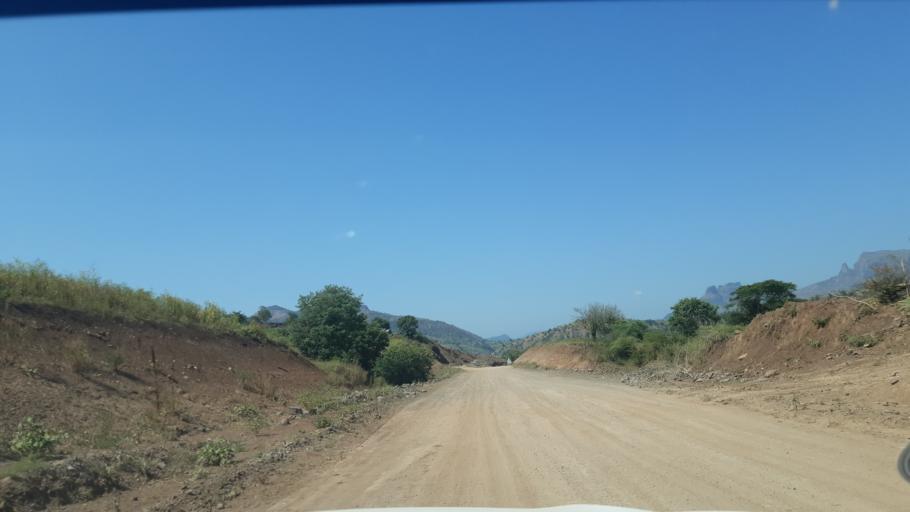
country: ET
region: Amhara
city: Dabat
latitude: 13.1931
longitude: 37.5653
